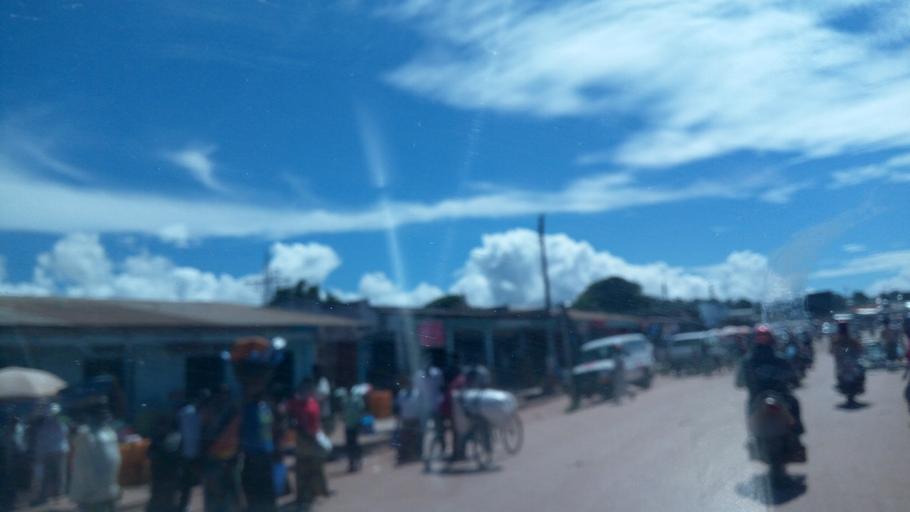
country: CD
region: Katanga
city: Kalemie
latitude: -5.9117
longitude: 29.1910
